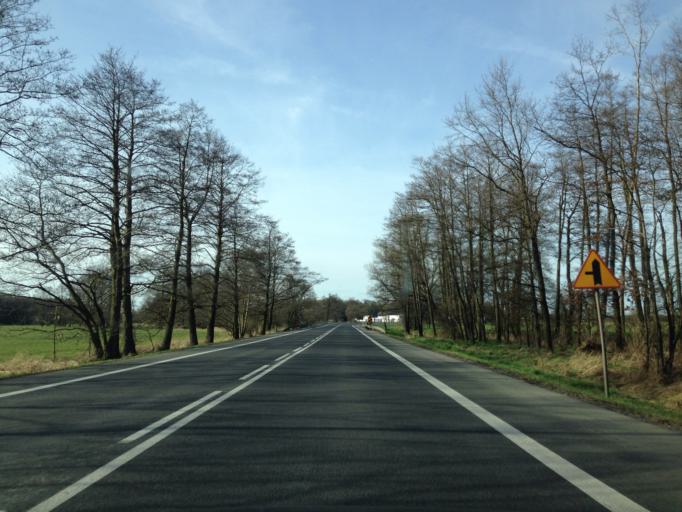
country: PL
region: Lodz Voivodeship
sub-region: Powiat kutnowski
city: Ostrowy
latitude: 52.3510
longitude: 19.1451
